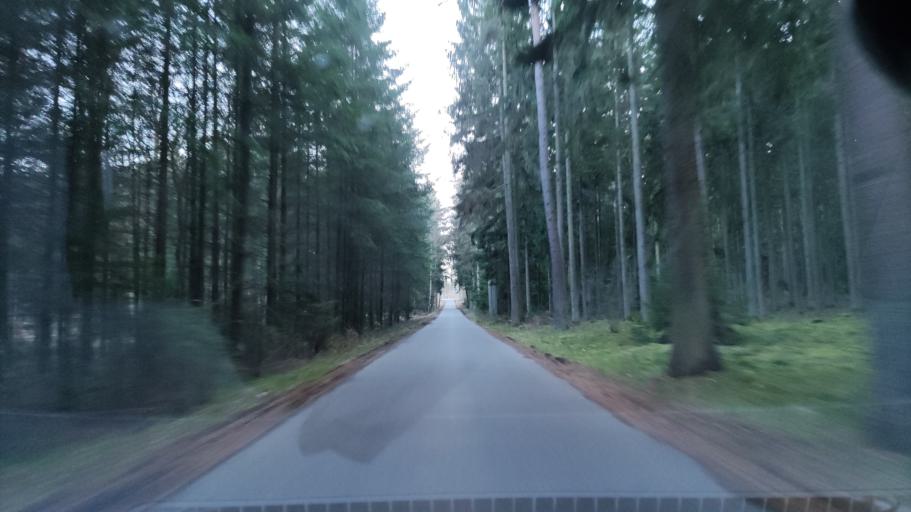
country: DE
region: Lower Saxony
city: Thomasburg
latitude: 53.1934
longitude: 10.6733
